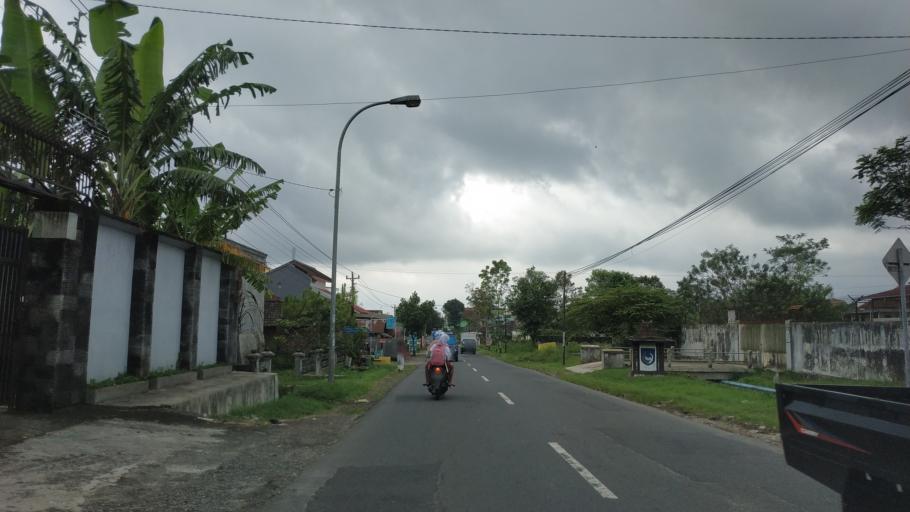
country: ID
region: Central Java
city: Magelang
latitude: -7.2856
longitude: 110.1134
